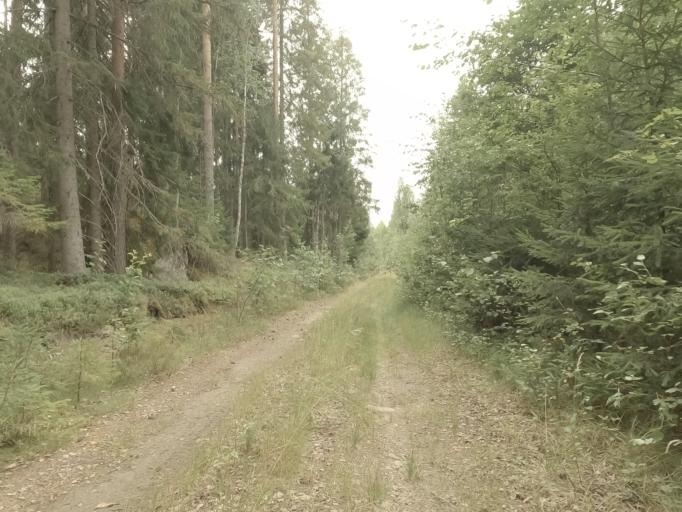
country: RU
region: Leningrad
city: Kamennogorsk
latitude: 61.0209
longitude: 29.1663
